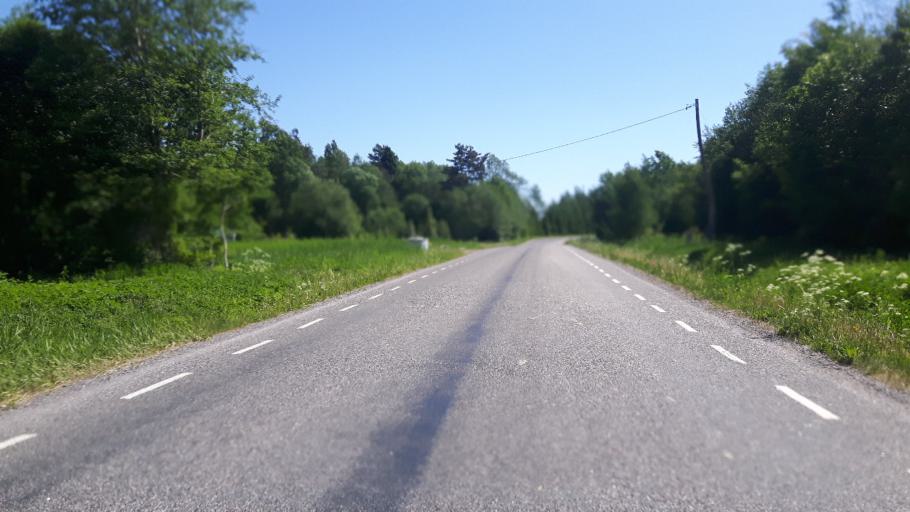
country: EE
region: Raplamaa
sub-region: Kohila vald
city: Kohila
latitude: 59.1799
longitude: 24.7259
